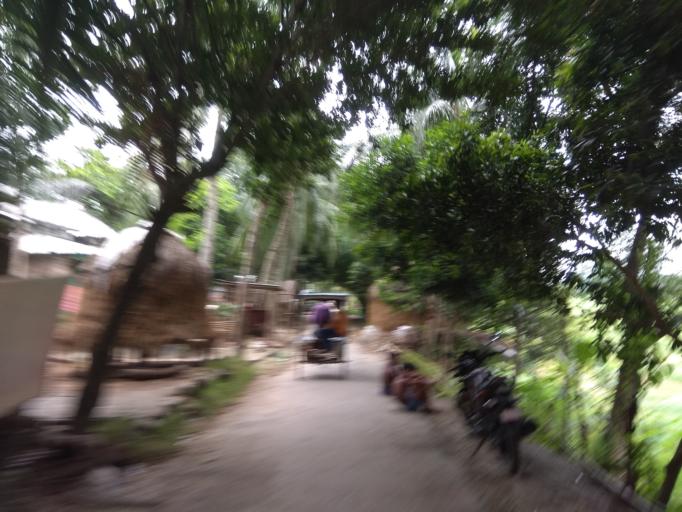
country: BD
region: Dhaka
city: Dohar
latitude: 23.4855
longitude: 90.0244
